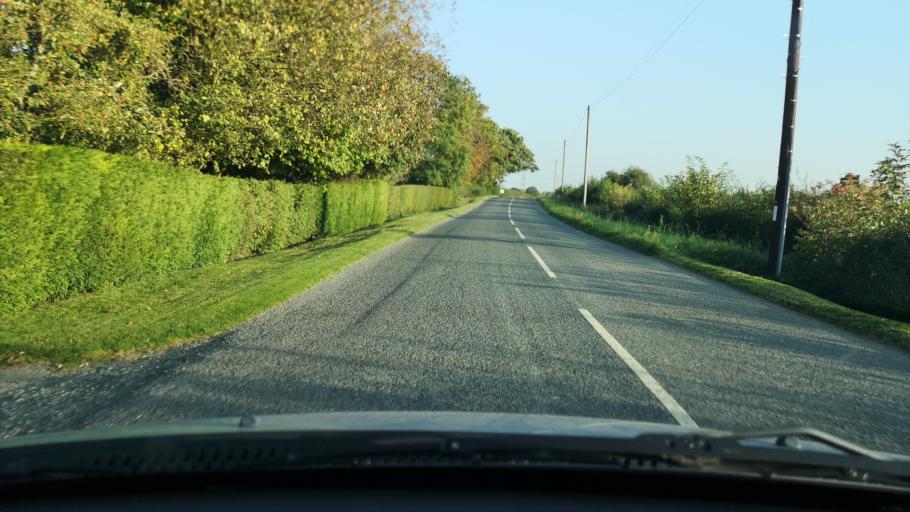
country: GB
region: England
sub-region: City and Borough of Wakefield
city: Knottingley
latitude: 53.6816
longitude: -1.2152
